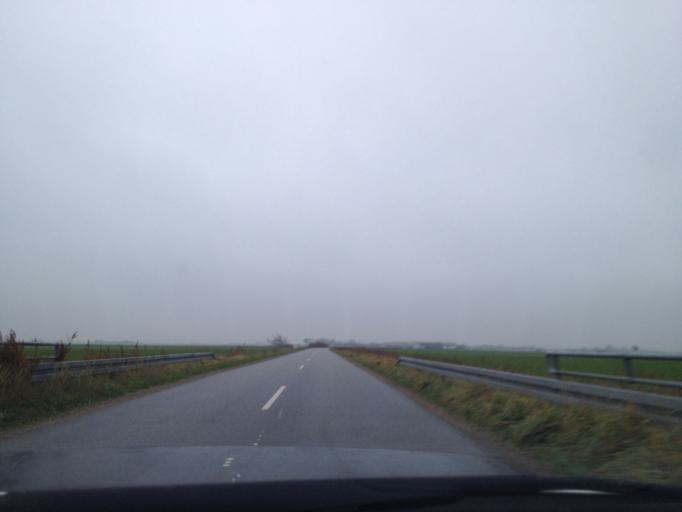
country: DK
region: South Denmark
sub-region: Tonder Kommune
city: Sherrebek
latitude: 55.1027
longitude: 8.7275
